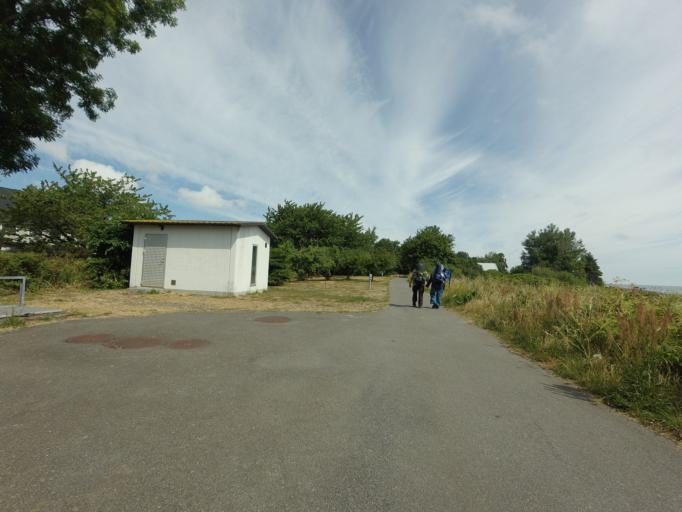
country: SE
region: Skane
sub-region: Simrishamns Kommun
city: Simrishamn
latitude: 55.5256
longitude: 14.3481
